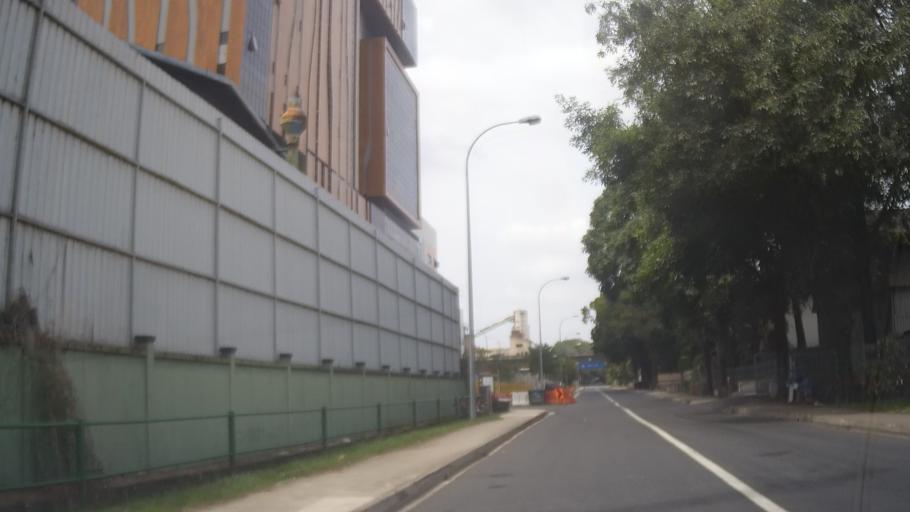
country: MY
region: Johor
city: Johor Bahru
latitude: 1.4127
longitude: 103.7510
